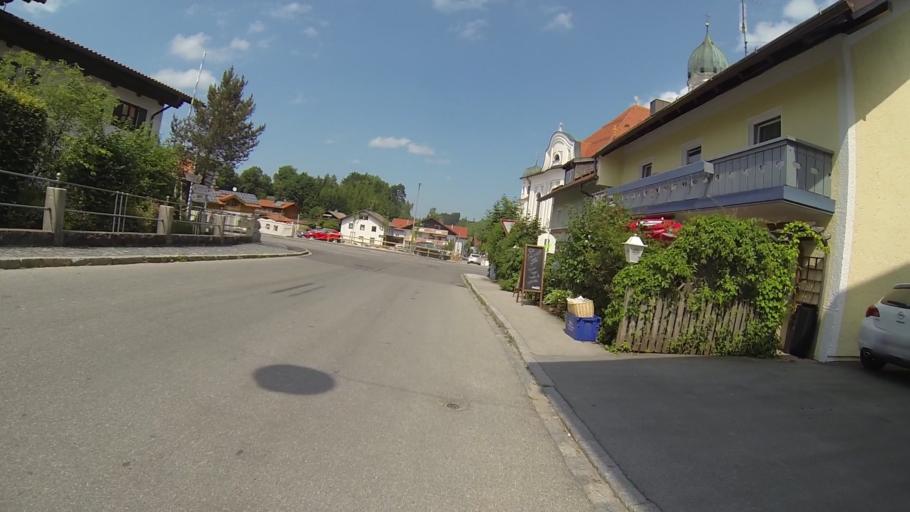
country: DE
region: Bavaria
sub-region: Swabia
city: Nesselwang
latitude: 47.6220
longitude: 10.4985
